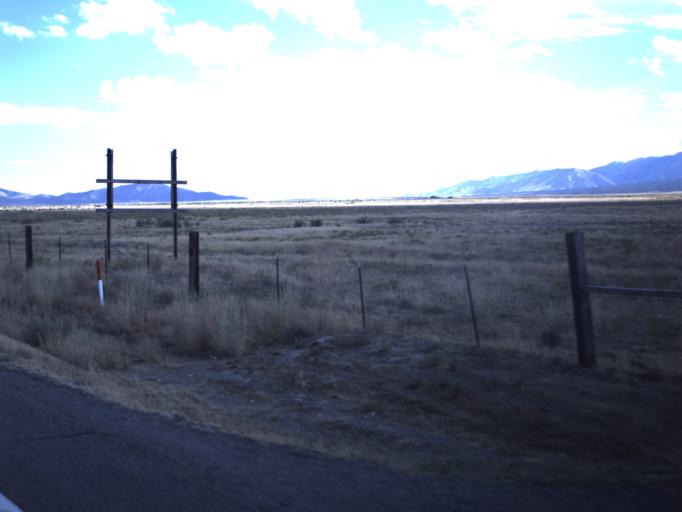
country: US
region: Utah
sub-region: Tooele County
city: Grantsville
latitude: 40.6143
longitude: -112.4968
